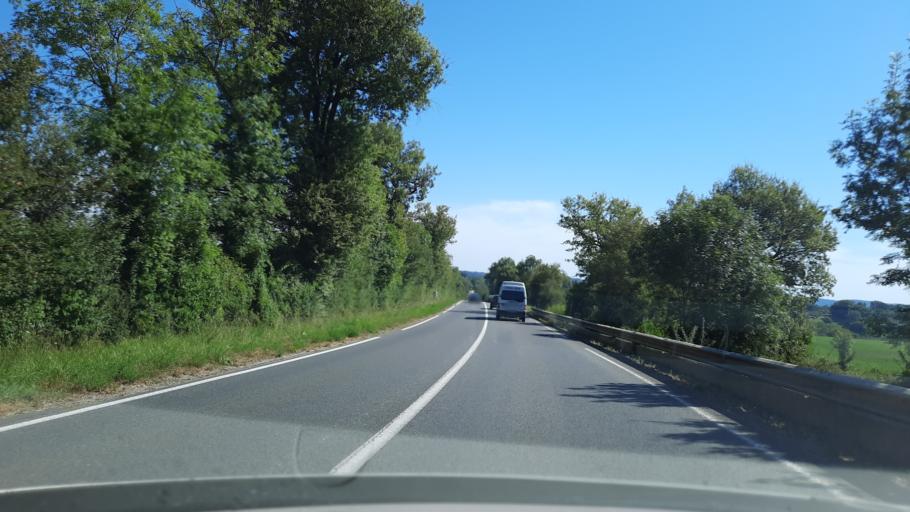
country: FR
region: Midi-Pyrenees
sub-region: Departement de l'Aveyron
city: Villefranche-de-Rouergue
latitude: 44.3519
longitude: 1.9772
